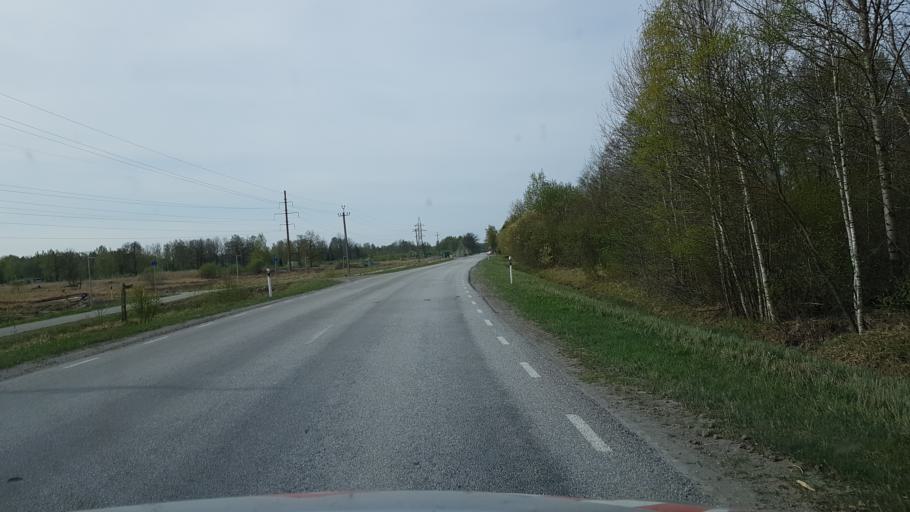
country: EE
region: Paernumaa
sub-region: Audru vald
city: Audru
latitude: 58.4163
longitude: 24.3113
